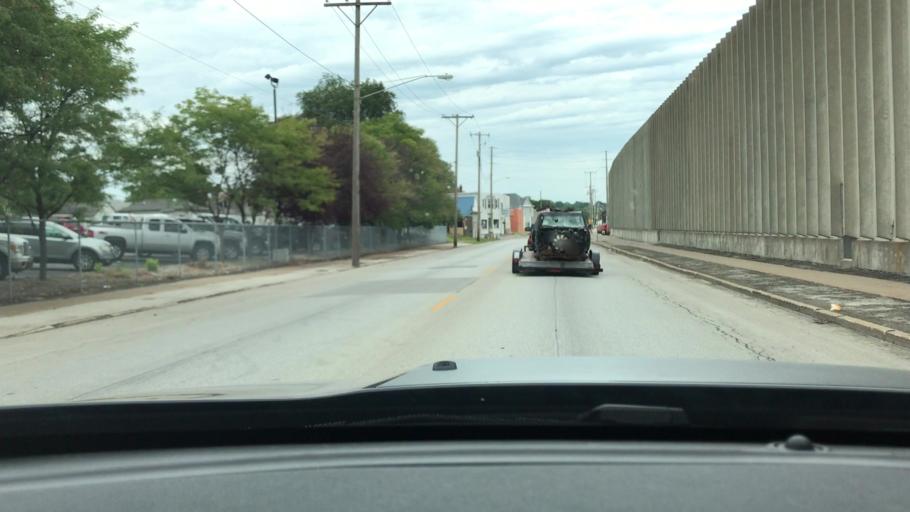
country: US
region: Illinois
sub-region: Rock Island County
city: Rock Island
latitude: 41.5174
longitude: -90.6064
